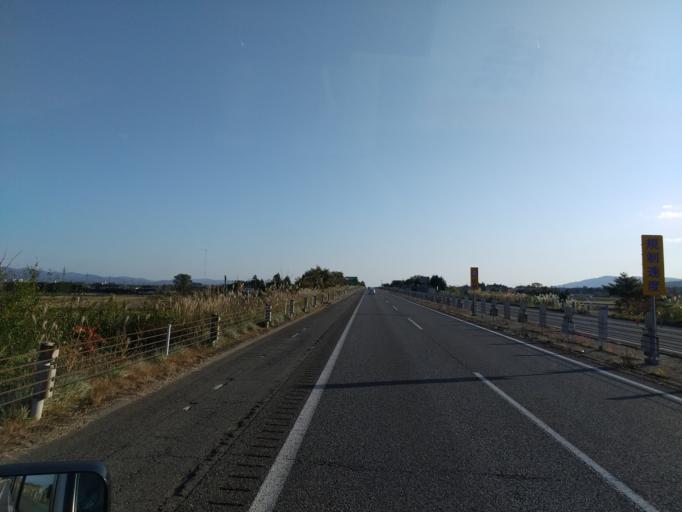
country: JP
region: Iwate
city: Morioka-shi
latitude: 39.6431
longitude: 141.1254
